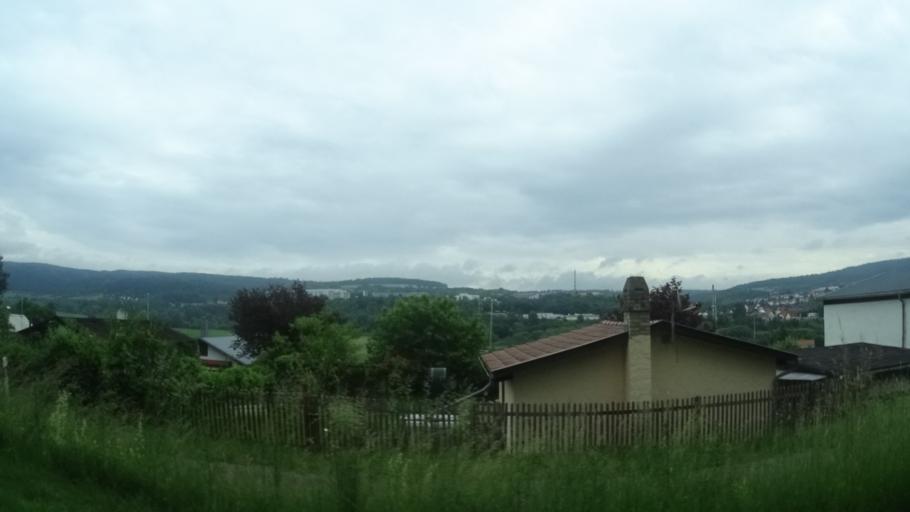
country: DE
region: Thuringia
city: Meiningen
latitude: 50.5870
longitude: 10.4027
